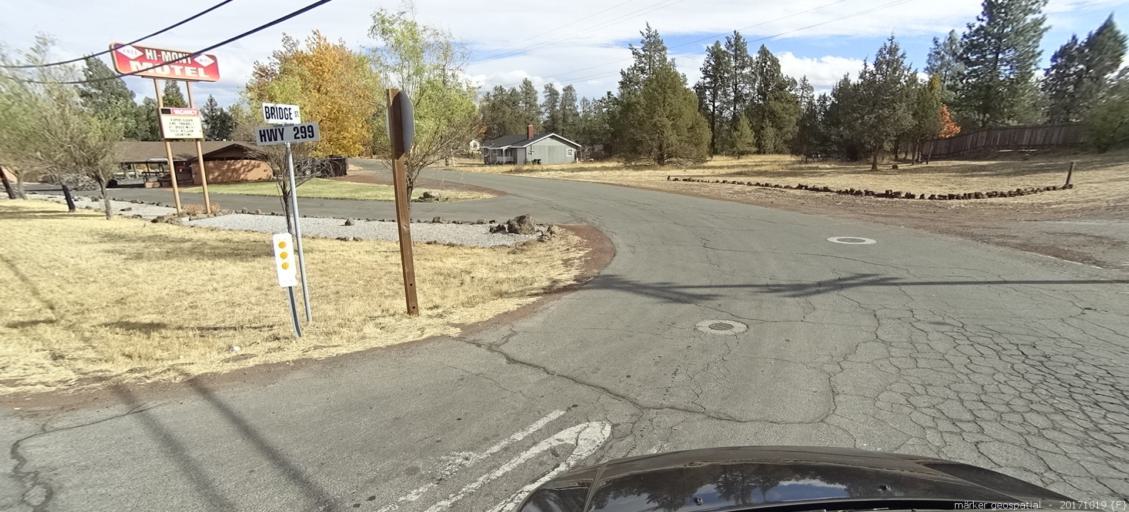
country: US
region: California
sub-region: Shasta County
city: Burney
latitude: 41.0011
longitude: -121.4466
